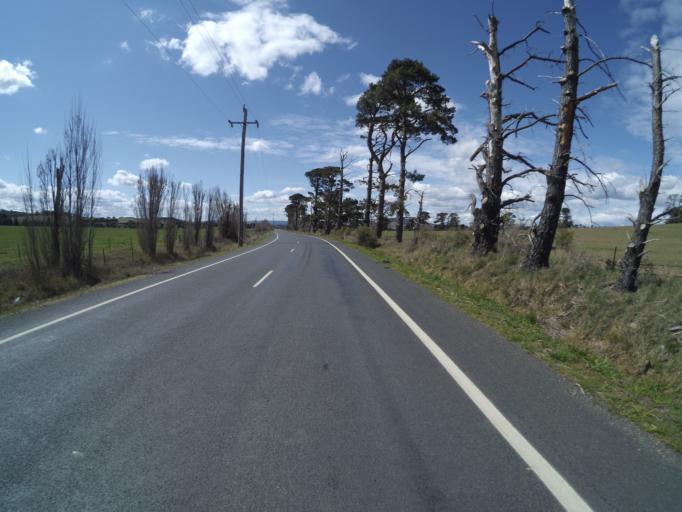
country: AU
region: New South Wales
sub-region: Goulburn Mulwaree
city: Goulburn
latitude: -34.7881
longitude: 149.7015
